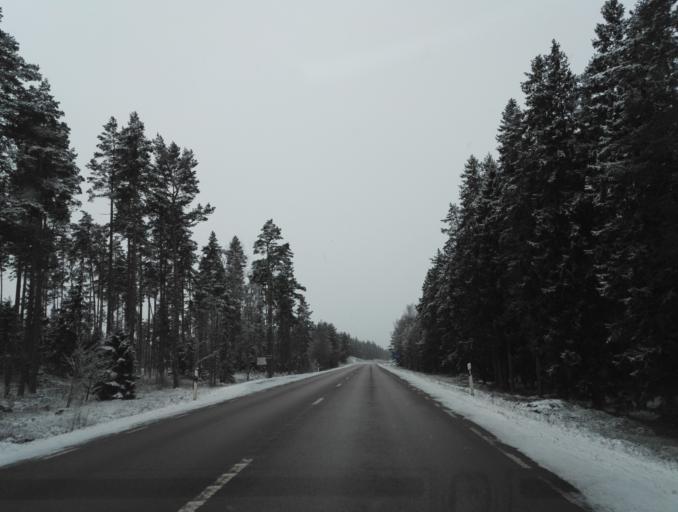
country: SE
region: Kronoberg
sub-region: Uppvidinge Kommun
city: Lenhovda
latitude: 57.1043
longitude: 15.2064
